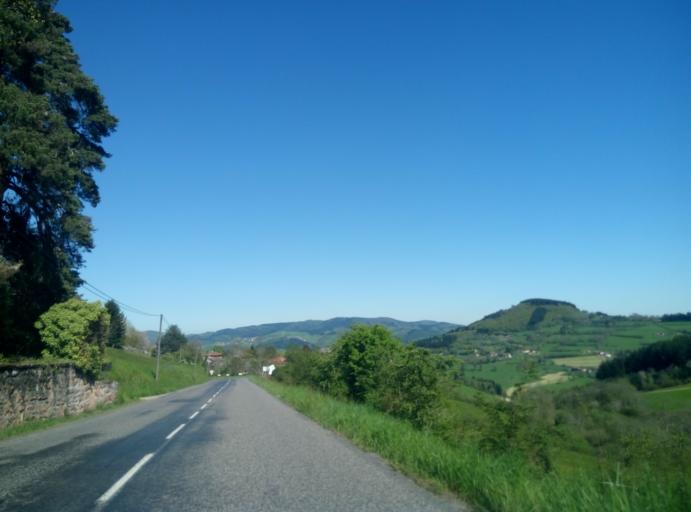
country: FR
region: Rhone-Alpes
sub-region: Departement du Rhone
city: Grandris
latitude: 46.0017
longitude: 4.4354
